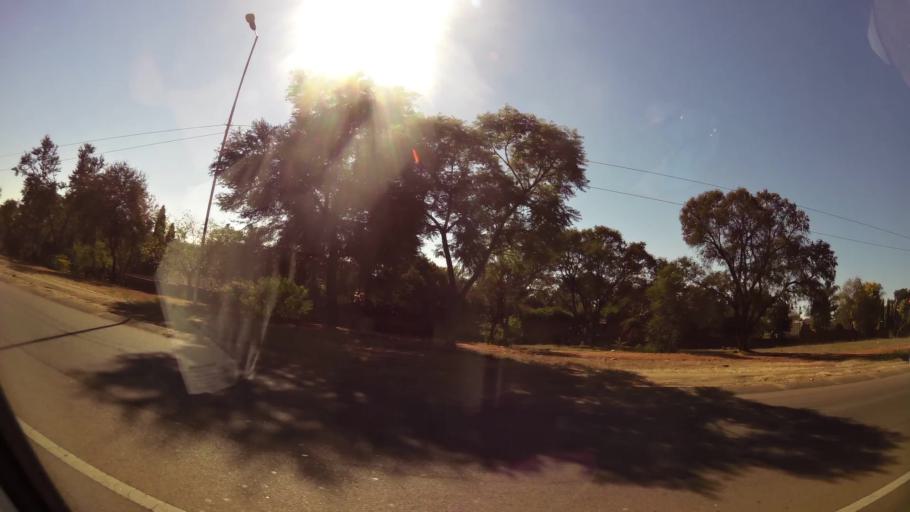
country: ZA
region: Gauteng
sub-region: City of Tshwane Metropolitan Municipality
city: Pretoria
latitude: -25.7949
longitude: 28.3134
